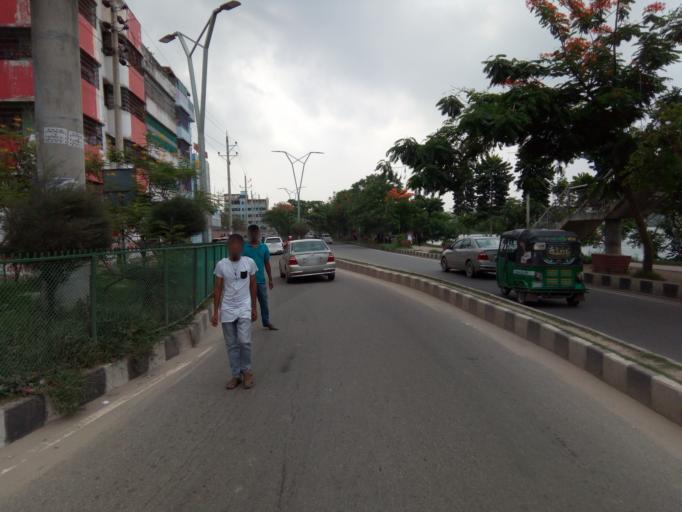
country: BD
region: Dhaka
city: Paltan
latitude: 23.7681
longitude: 90.4217
